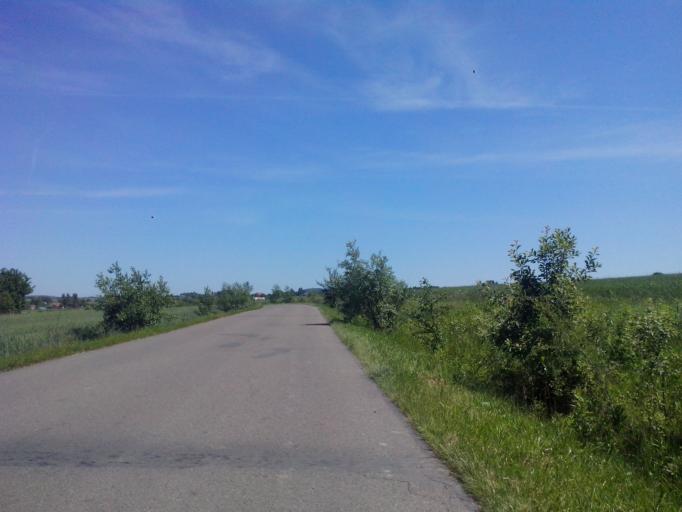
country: PL
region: Subcarpathian Voivodeship
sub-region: Powiat strzyzowski
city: Wisniowa
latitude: 49.8560
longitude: 21.6926
